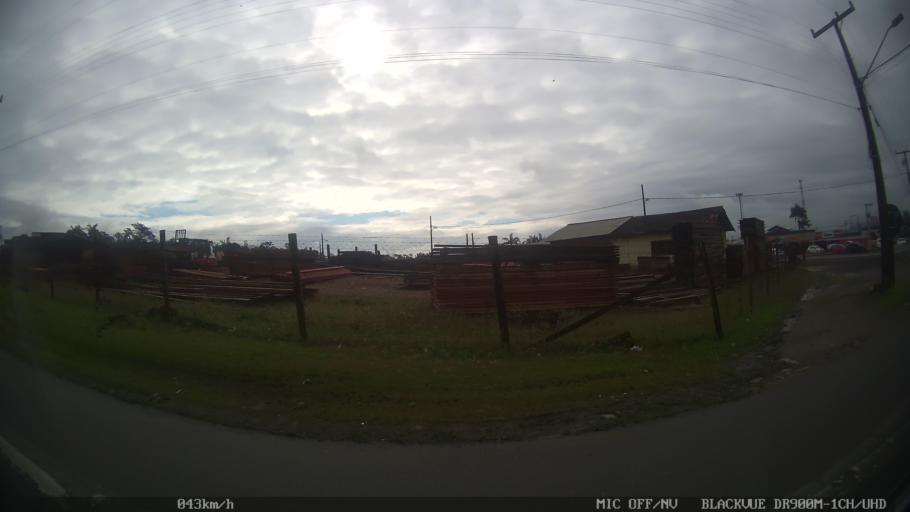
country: BR
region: Santa Catarina
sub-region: Joinville
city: Joinville
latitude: -26.0280
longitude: -48.8608
